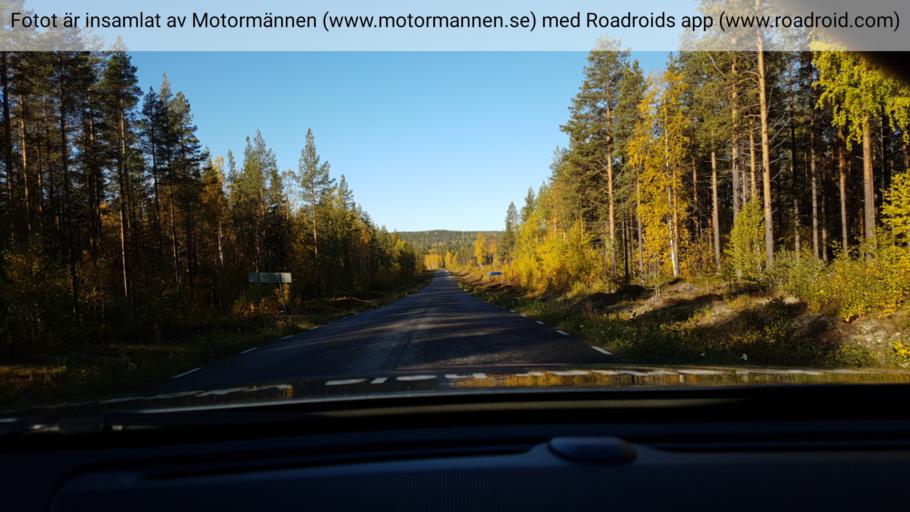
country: SE
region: Norrbotten
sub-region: Alvsbyns Kommun
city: AElvsbyn
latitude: 66.2777
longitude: 21.1166
